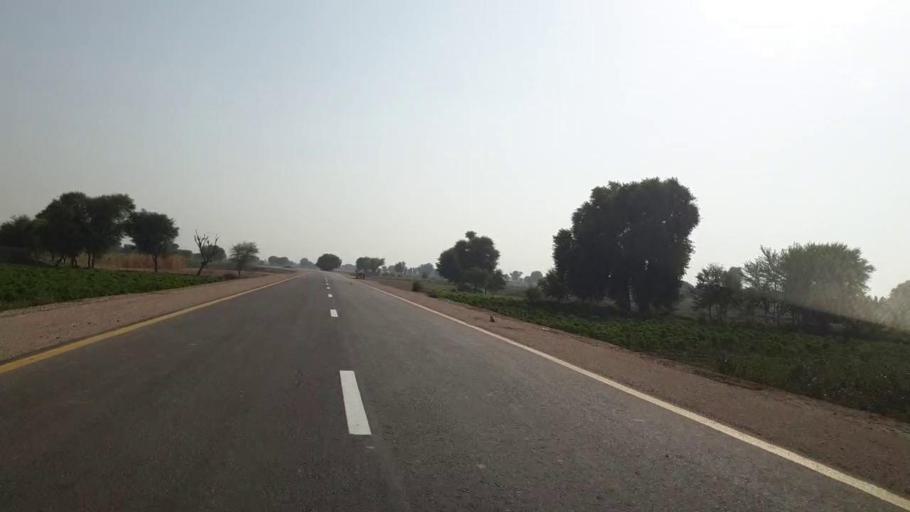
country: PK
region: Sindh
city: Bhan
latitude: 26.5106
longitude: 67.7848
